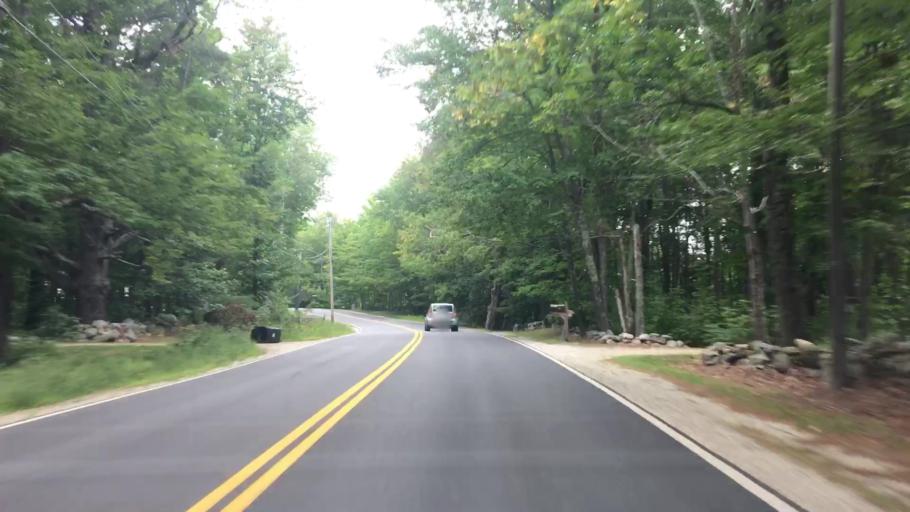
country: US
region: Maine
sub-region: Cumberland County
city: Cumberland Center
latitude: 43.8806
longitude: -70.2475
